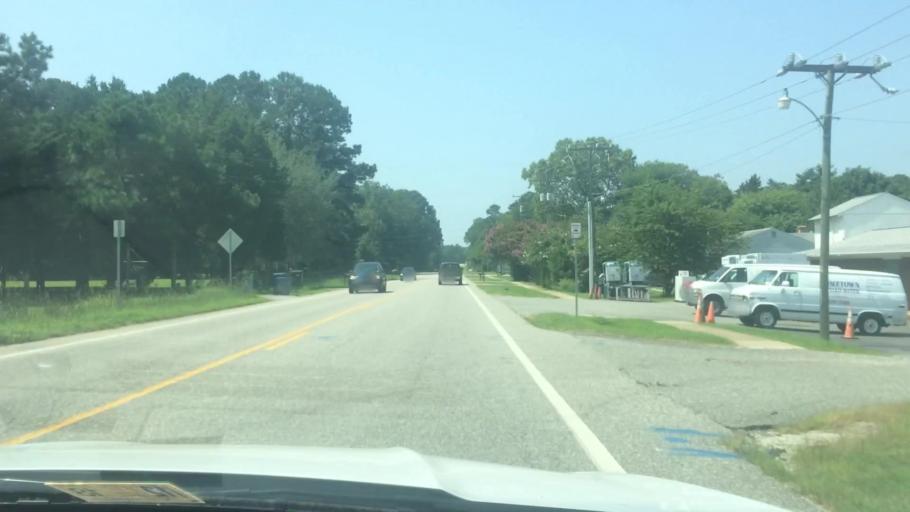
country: US
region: Virginia
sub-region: James City County
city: Williamsburg
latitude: 37.3377
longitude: -76.7677
